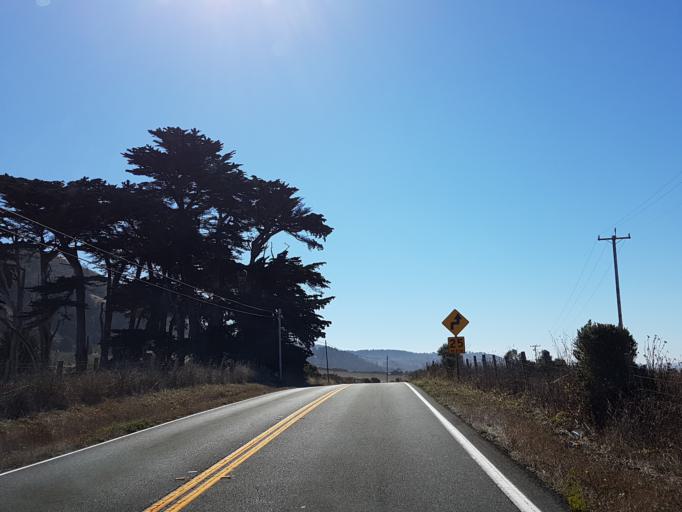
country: US
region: California
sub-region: Mendocino County
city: Boonville
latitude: 39.0777
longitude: -123.6950
